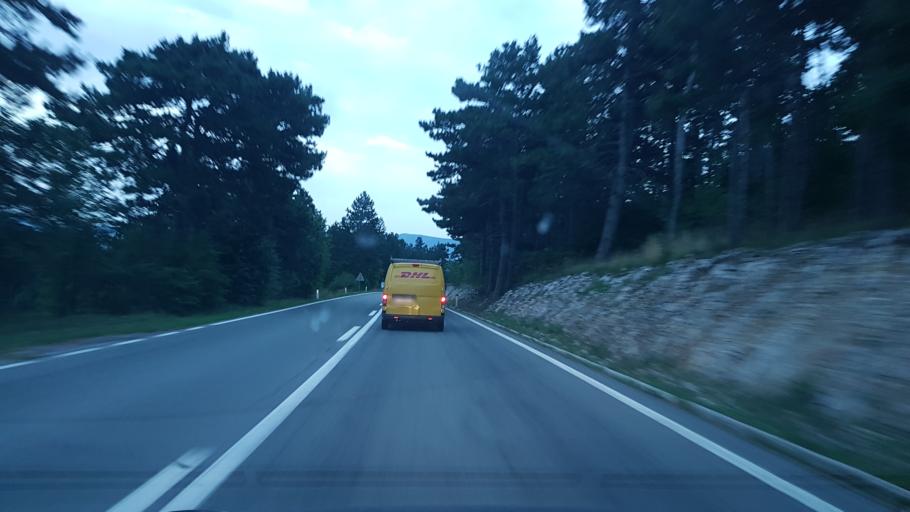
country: SI
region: Divaca
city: Divaca
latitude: 45.6972
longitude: 13.9858
